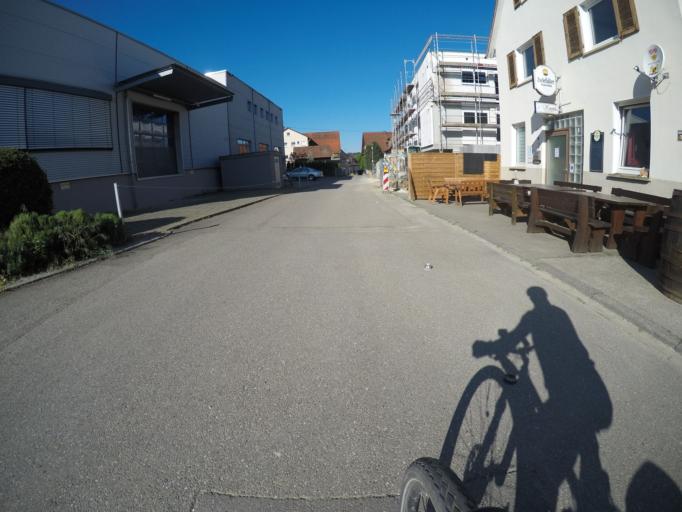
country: DE
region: Baden-Wuerttemberg
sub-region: Regierungsbezirk Stuttgart
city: Neckartailfingen
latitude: 48.6226
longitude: 9.2427
